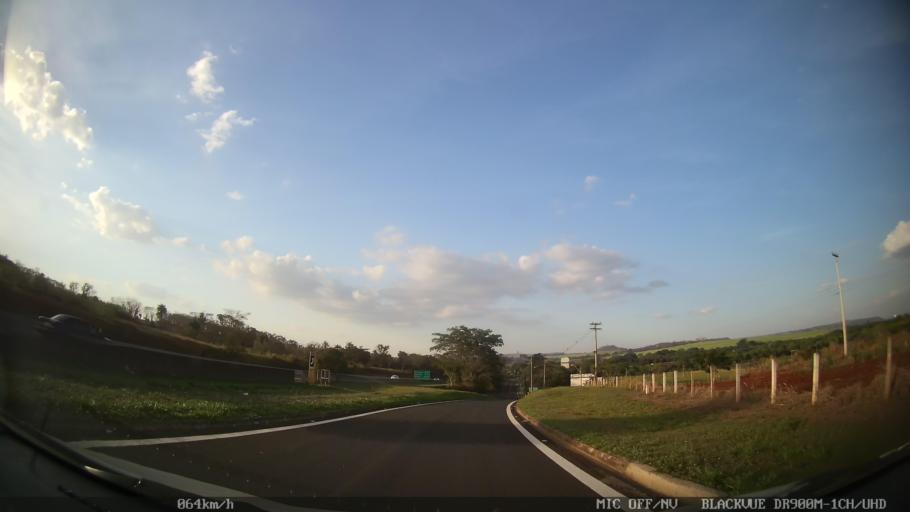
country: BR
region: Sao Paulo
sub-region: Ribeirao Preto
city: Ribeirao Preto
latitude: -21.1040
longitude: -47.7673
